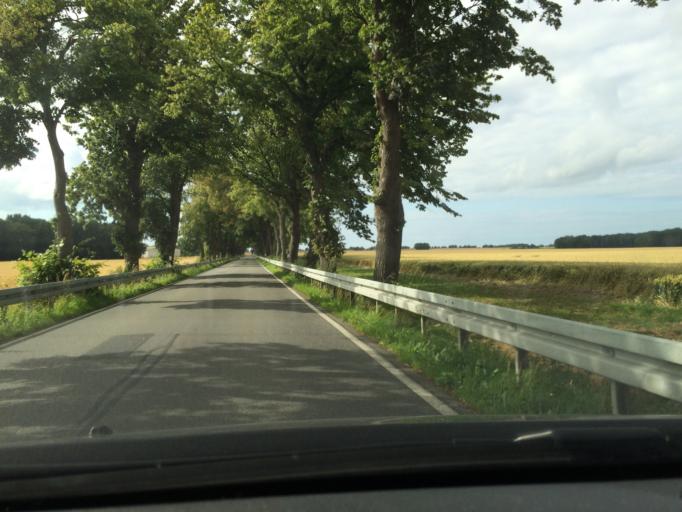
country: DE
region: Mecklenburg-Vorpommern
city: Prohn
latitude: 54.3853
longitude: 13.0017
